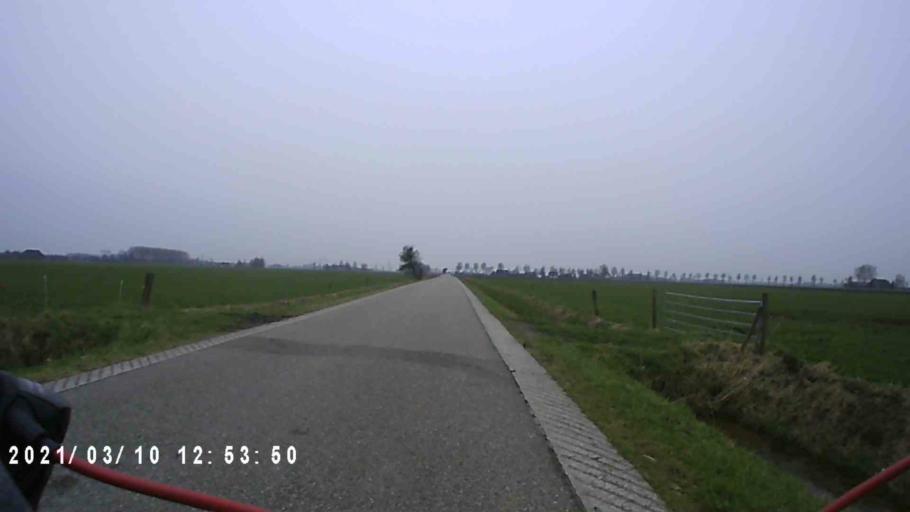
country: NL
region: Groningen
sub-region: Gemeente Bedum
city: Bedum
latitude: 53.2969
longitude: 6.6287
